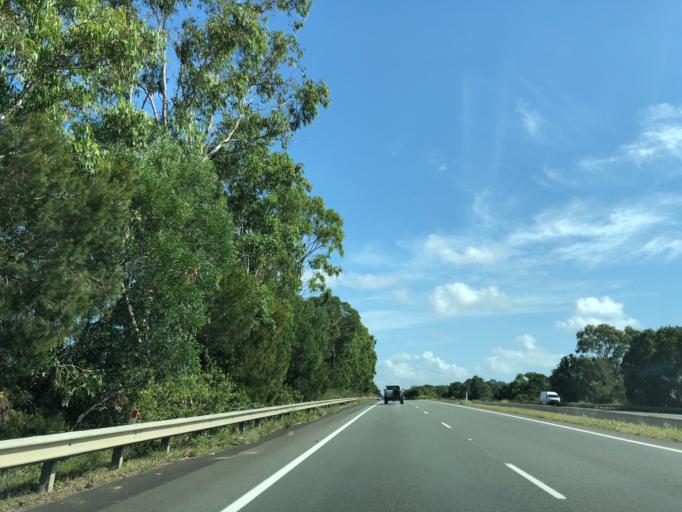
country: AU
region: New South Wales
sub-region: Byron Shire
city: Brunswick Heads
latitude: -28.6062
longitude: 153.5461
